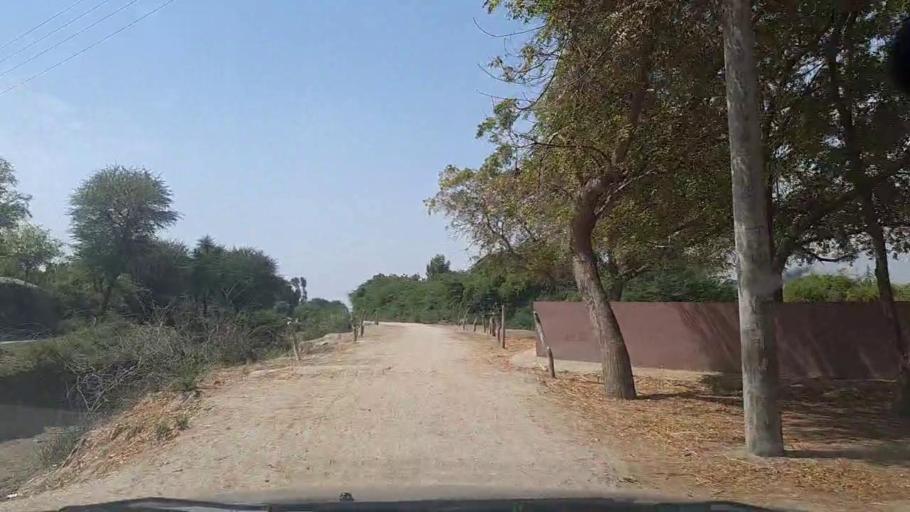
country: PK
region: Sindh
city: Mirpur Batoro
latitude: 24.6532
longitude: 68.1720
